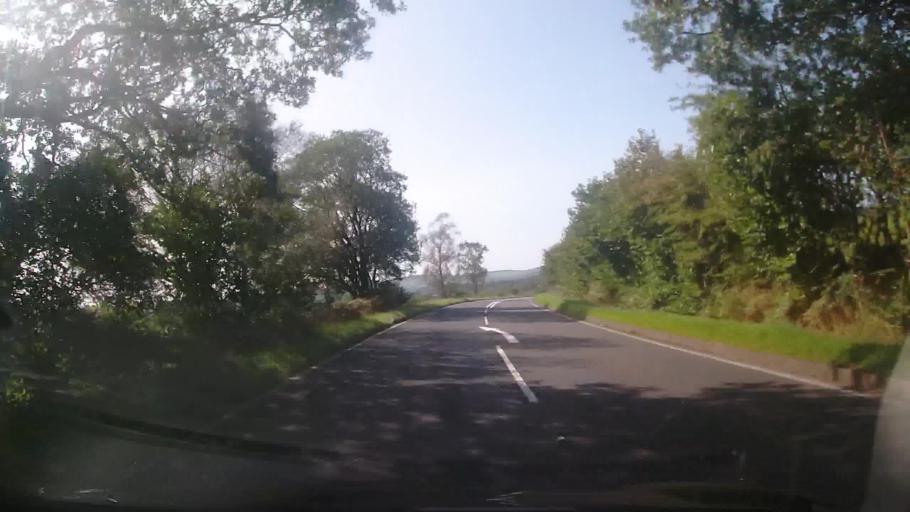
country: GB
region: Wales
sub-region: Carmarthenshire
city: Llandovery
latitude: 52.1158
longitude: -3.6220
